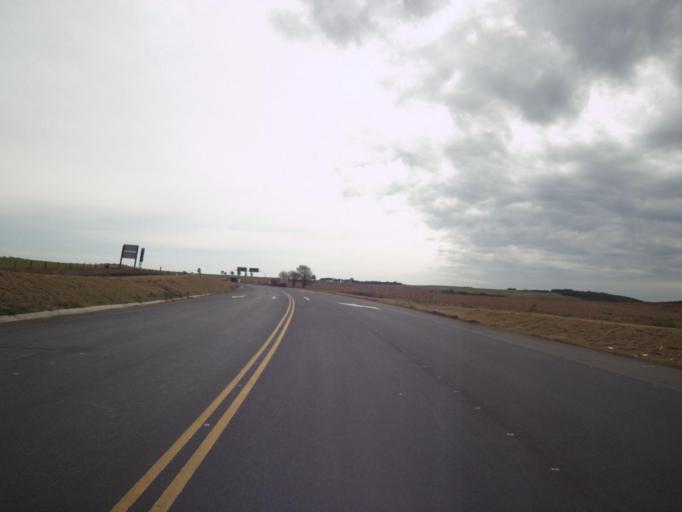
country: BR
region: Santa Catarina
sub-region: Cacador
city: Cacador
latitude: -26.6064
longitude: -51.4796
